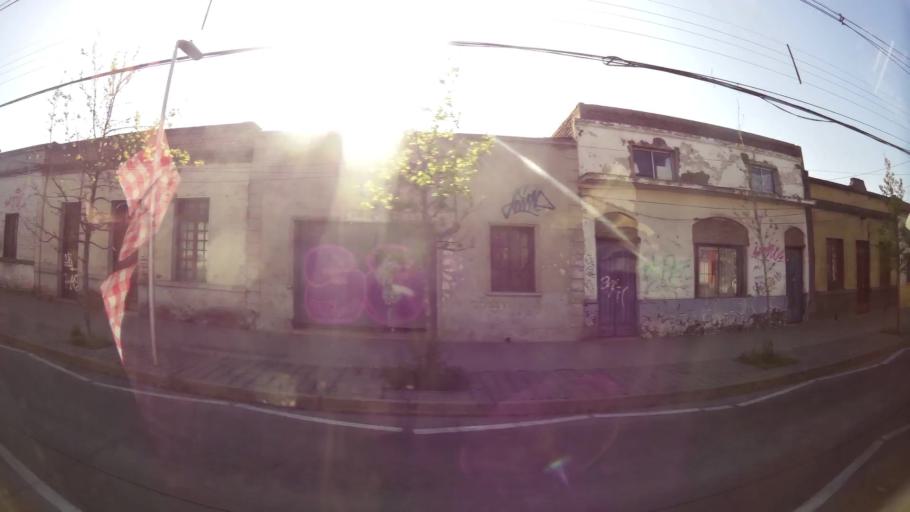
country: CL
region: Santiago Metropolitan
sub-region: Provincia de Santiago
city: Santiago
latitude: -33.4700
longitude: -70.6335
